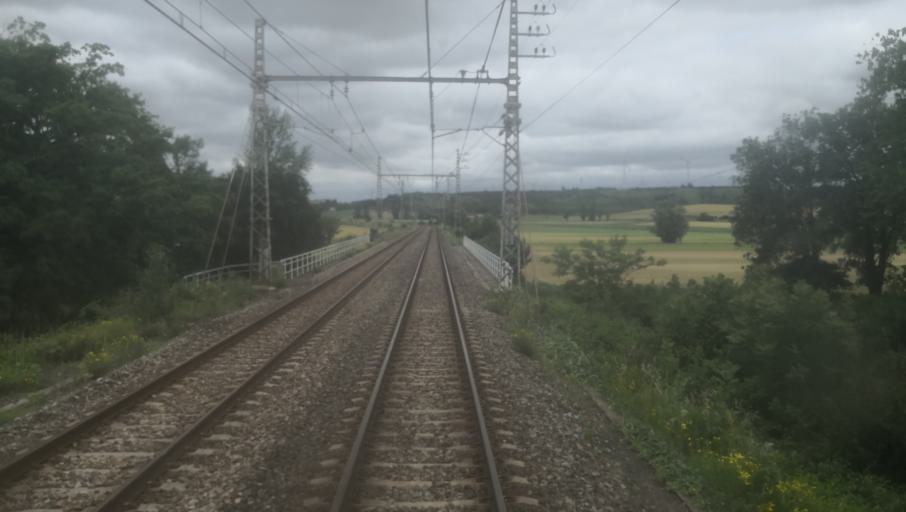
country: FR
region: Midi-Pyrenees
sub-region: Departement de la Haute-Garonne
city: Avignonet-Lauragais
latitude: 43.3570
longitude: 1.8065
